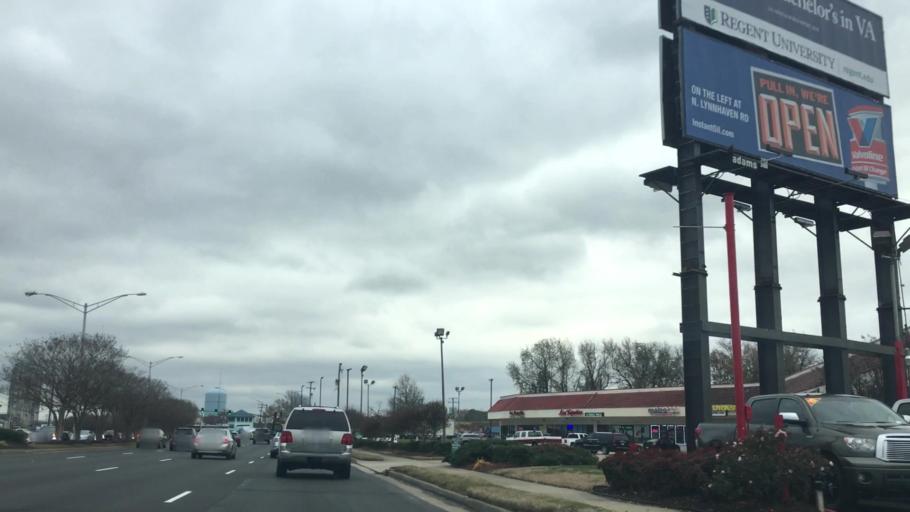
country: US
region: Virginia
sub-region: City of Chesapeake
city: Chesapeake
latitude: 36.8447
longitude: -76.1544
